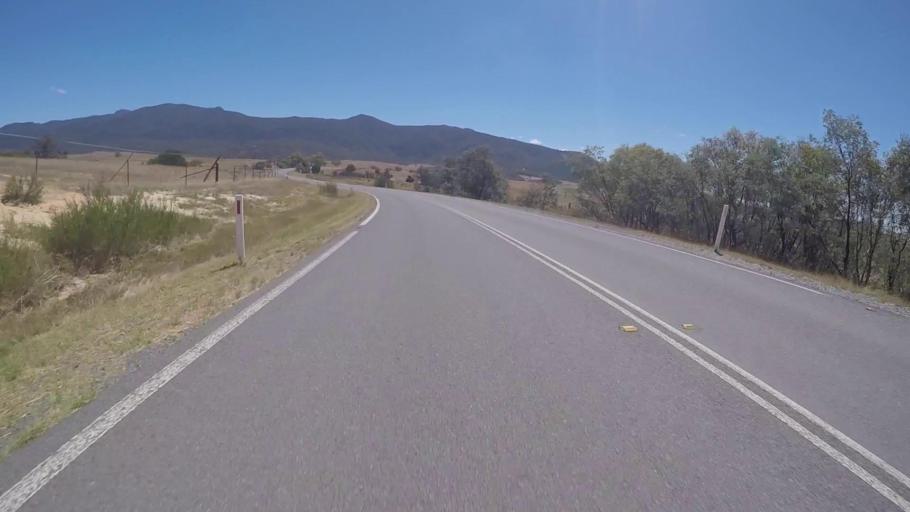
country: AU
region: Australian Capital Territory
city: Macarthur
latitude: -35.4376
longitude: 148.9511
